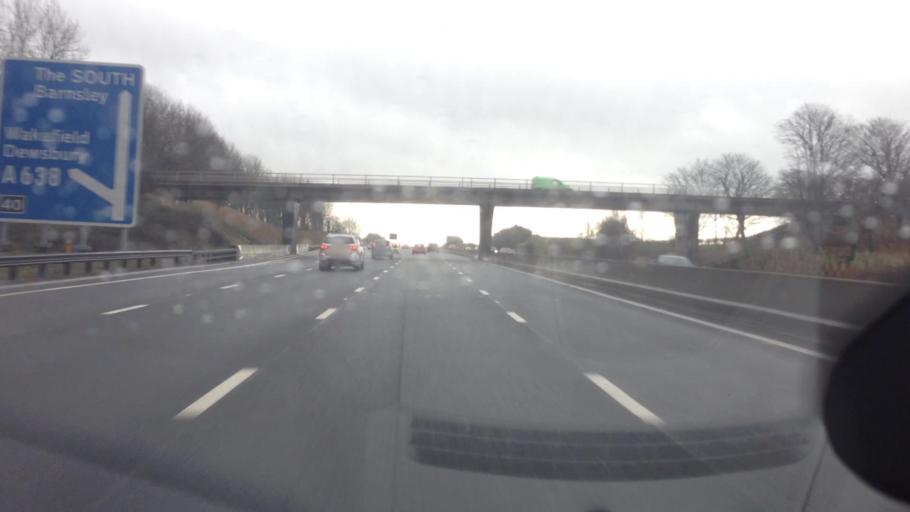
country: GB
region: England
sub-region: City and Borough of Wakefield
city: Ossett
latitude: 53.6906
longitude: -1.5565
